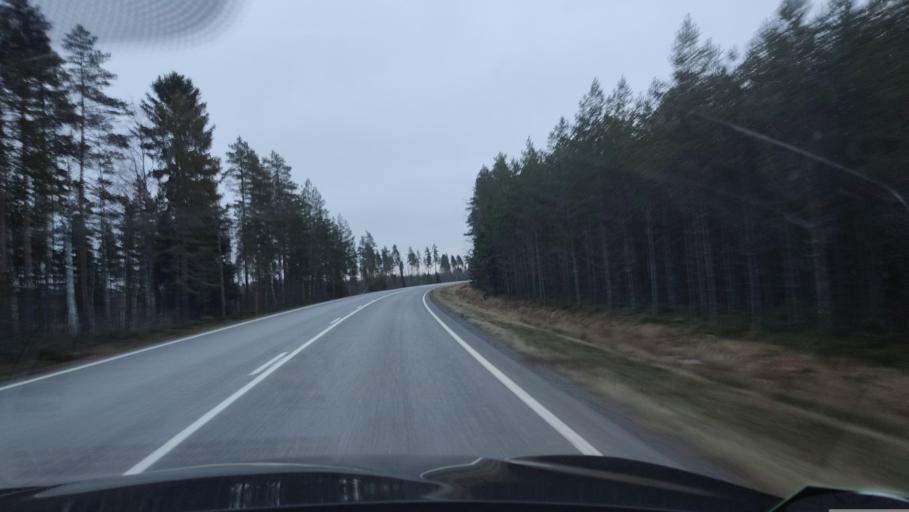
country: FI
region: Southern Ostrobothnia
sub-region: Suupohja
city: Isojoki
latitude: 62.3449
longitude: 21.9656
